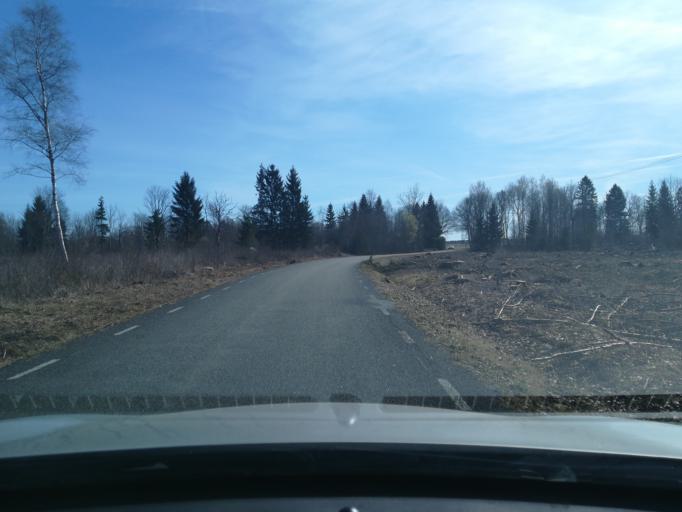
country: EE
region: Harju
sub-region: Saku vald
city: Saku
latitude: 59.2941
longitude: 24.6149
